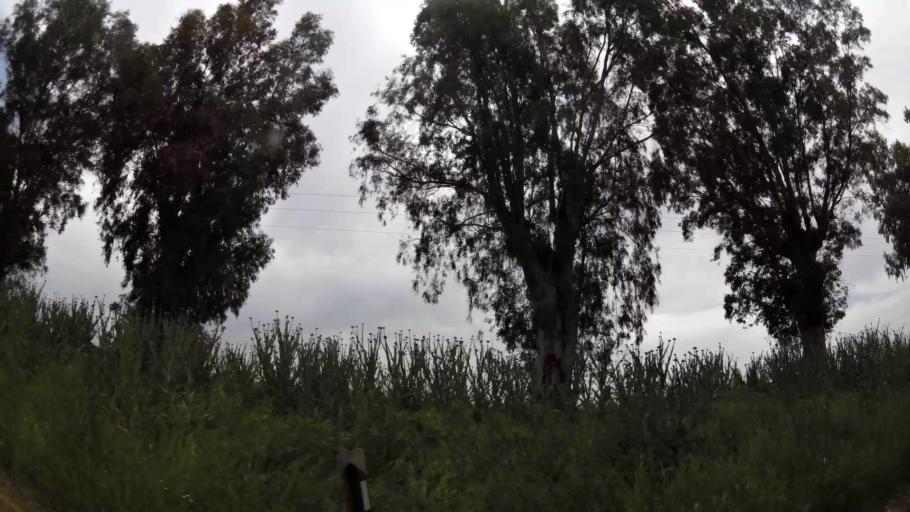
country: MA
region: Rabat-Sale-Zemmour-Zaer
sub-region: Khemisset
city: Tiflet
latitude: 33.8648
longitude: -6.2731
